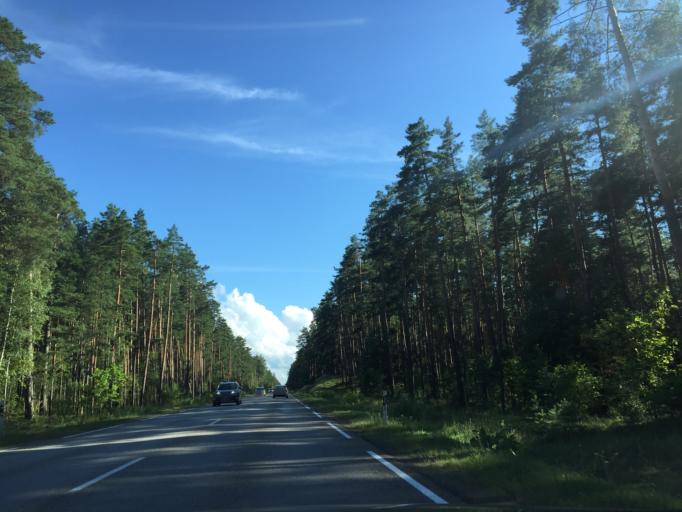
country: LV
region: Riga
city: Jaunciems
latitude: 57.0681
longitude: 24.1575
